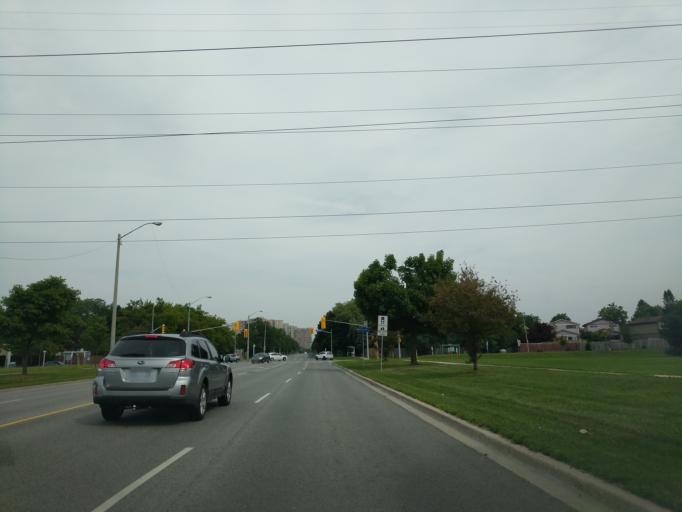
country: CA
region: Ontario
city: Scarborough
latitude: 43.8056
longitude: -79.3206
